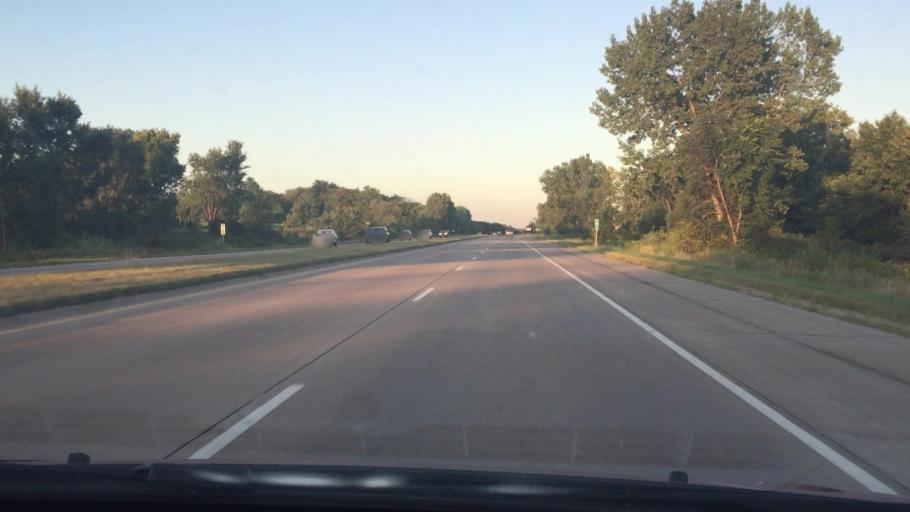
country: US
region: Iowa
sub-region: Muscatine County
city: Muscatine
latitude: 41.4527
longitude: -91.0649
